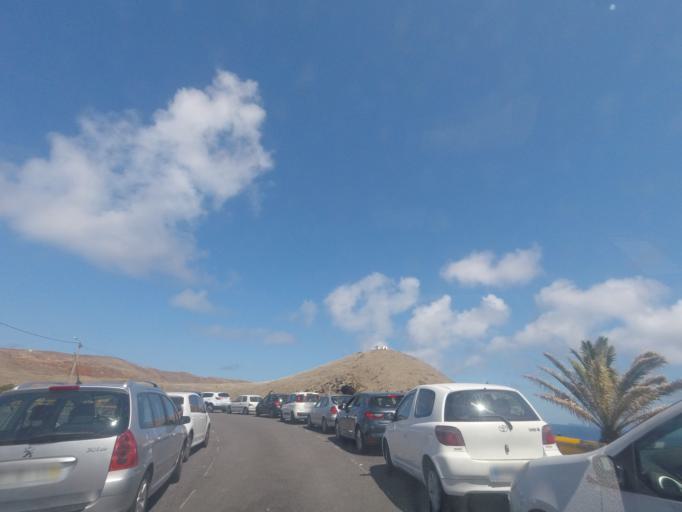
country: PT
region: Madeira
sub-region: Machico
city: Canical
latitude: 32.7438
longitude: -16.7167
